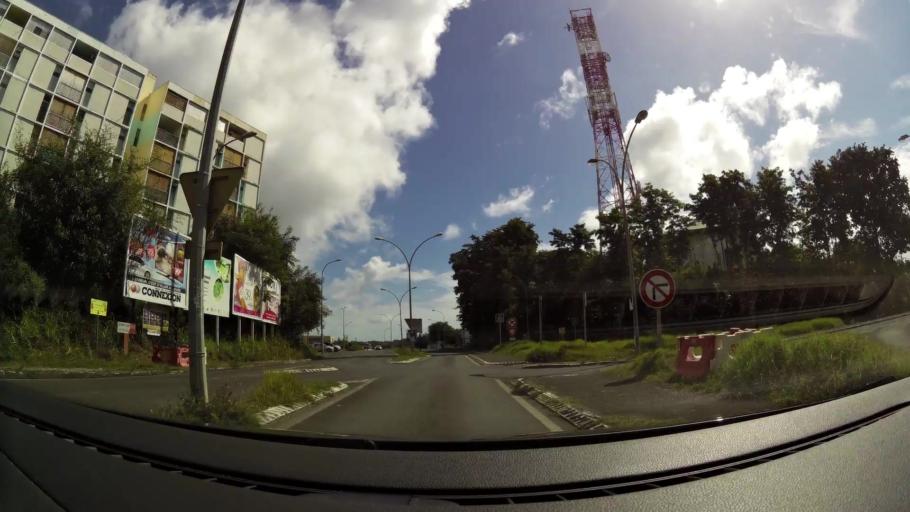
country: GP
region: Guadeloupe
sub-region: Guadeloupe
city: Pointe-a-Pitre
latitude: 16.2498
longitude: -61.5375
